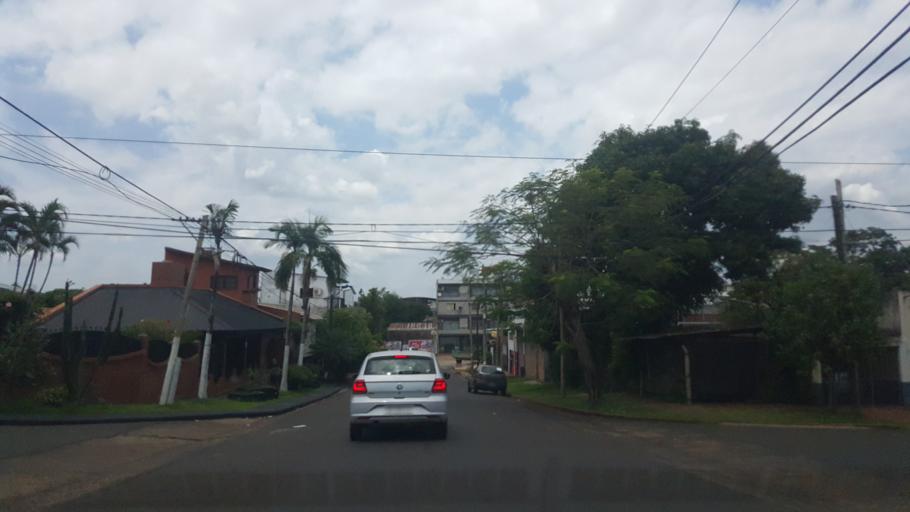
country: AR
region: Misiones
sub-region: Departamento de Capital
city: Posadas
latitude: -27.3802
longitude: -55.8980
